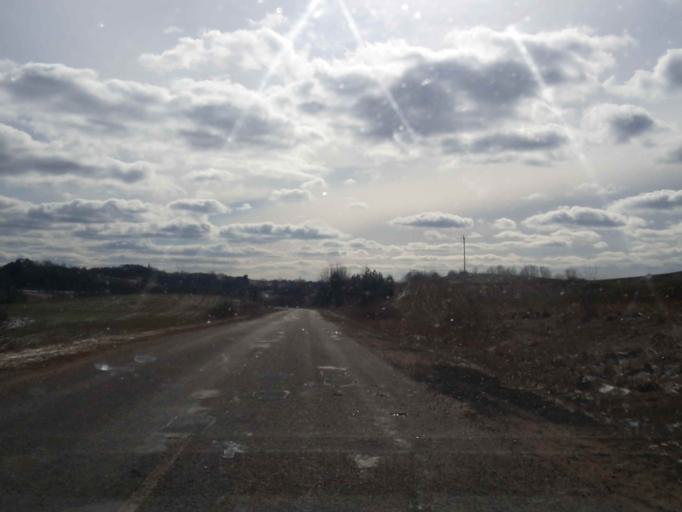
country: BY
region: Vitebsk
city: Mosar
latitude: 55.0810
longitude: 27.2192
